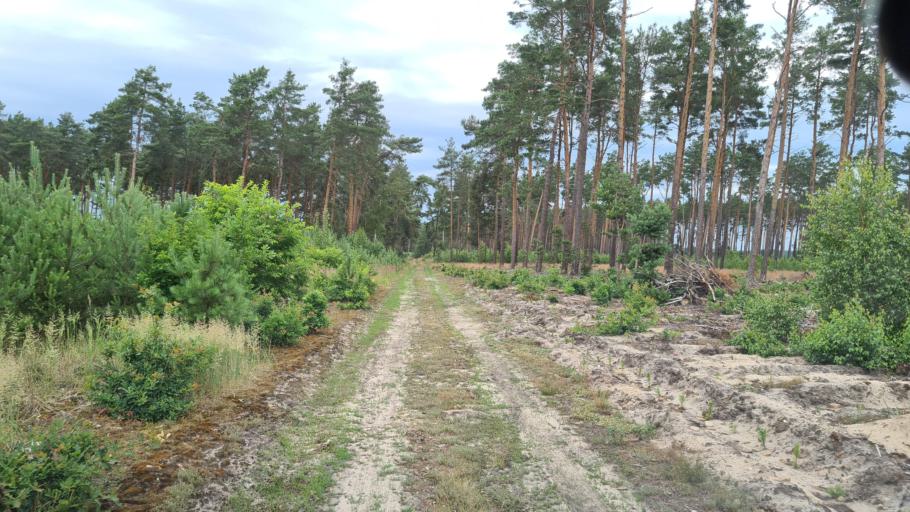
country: DE
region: Brandenburg
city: Crinitz
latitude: 51.7190
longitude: 13.8439
